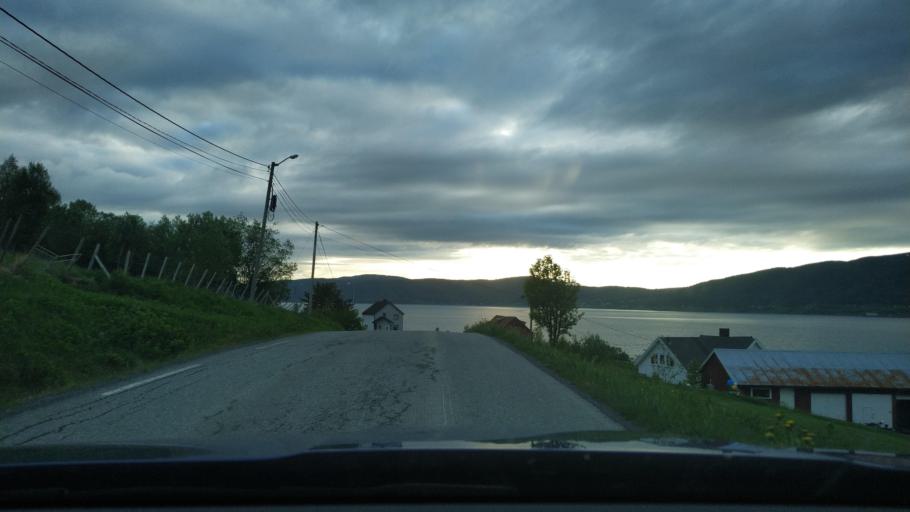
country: NO
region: Troms
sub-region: Tranoy
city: Vangsvika
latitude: 69.1272
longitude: 17.8500
